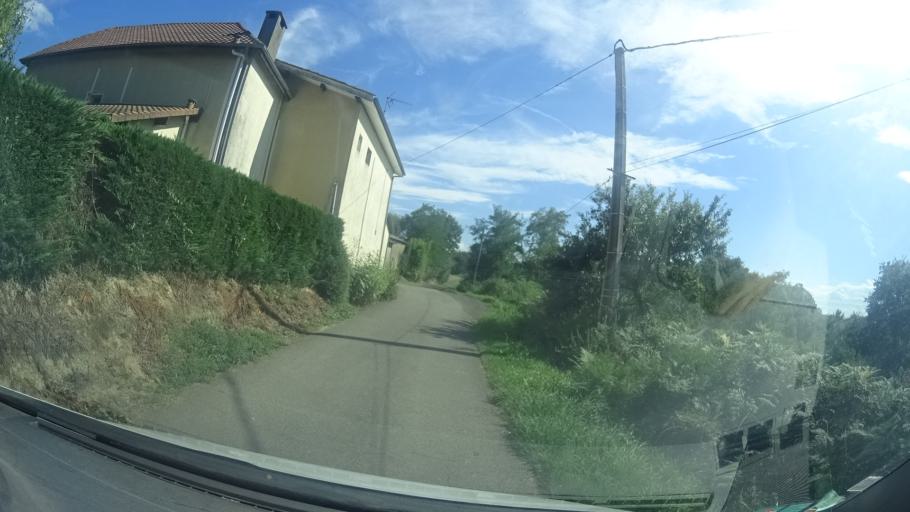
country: FR
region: Aquitaine
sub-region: Departement des Pyrenees-Atlantiques
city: Mont
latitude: 43.5016
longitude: -0.6760
